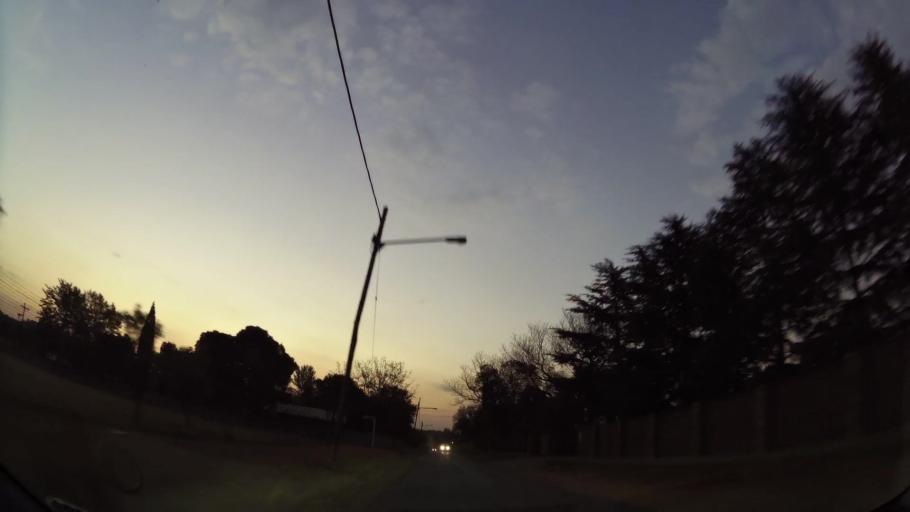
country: ZA
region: Gauteng
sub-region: Ekurhuleni Metropolitan Municipality
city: Benoni
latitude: -26.1313
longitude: 28.3112
